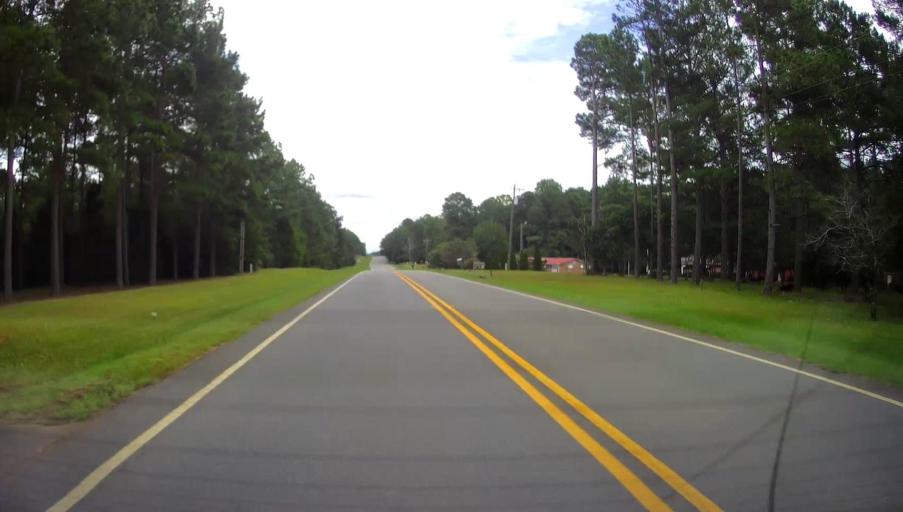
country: US
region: Georgia
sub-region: Schley County
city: Ellaville
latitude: 32.2587
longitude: -84.2286
